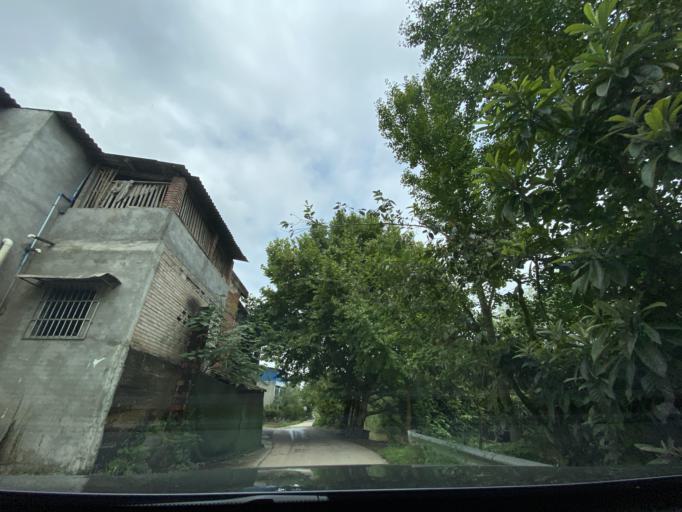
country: CN
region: Sichuan
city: Jiancheng
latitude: 30.3996
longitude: 104.5673
